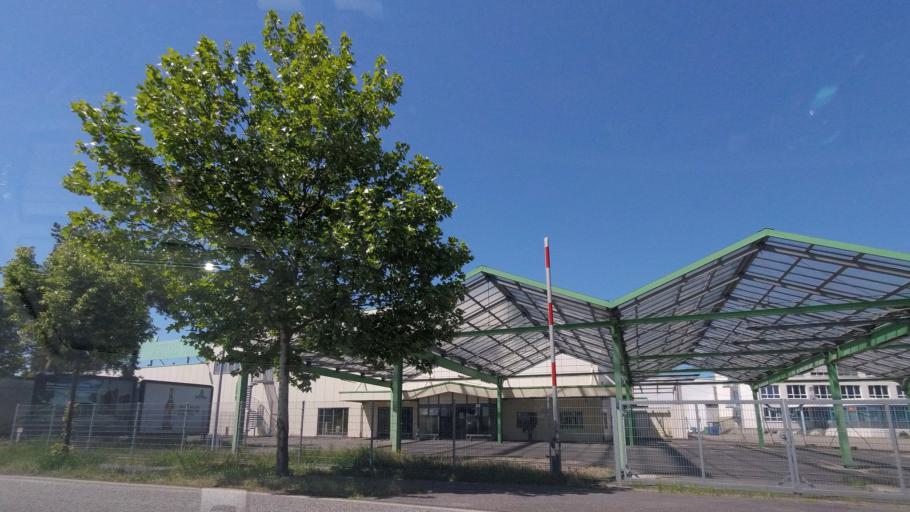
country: DE
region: Brandenburg
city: Ludwigsfelde
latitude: 52.2996
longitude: 13.2735
